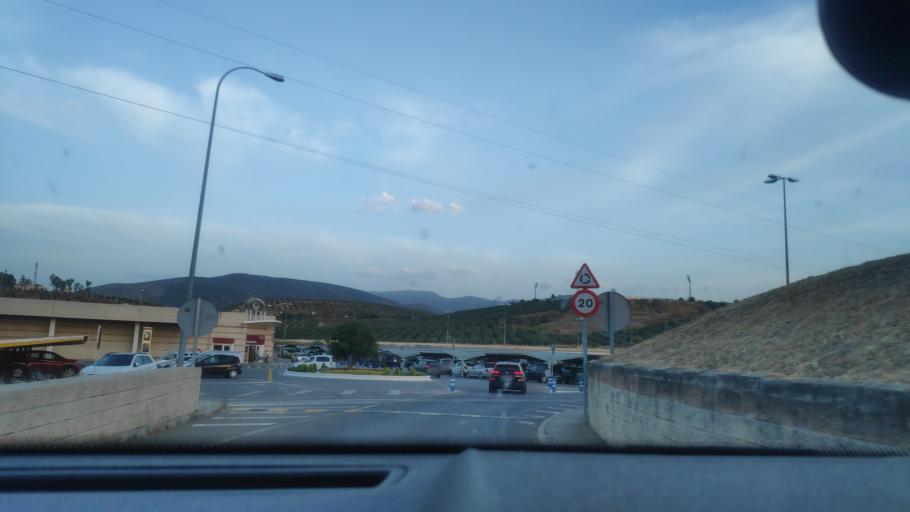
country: ES
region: Andalusia
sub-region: Provincia de Jaen
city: Jaen
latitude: 37.7822
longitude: -3.7692
